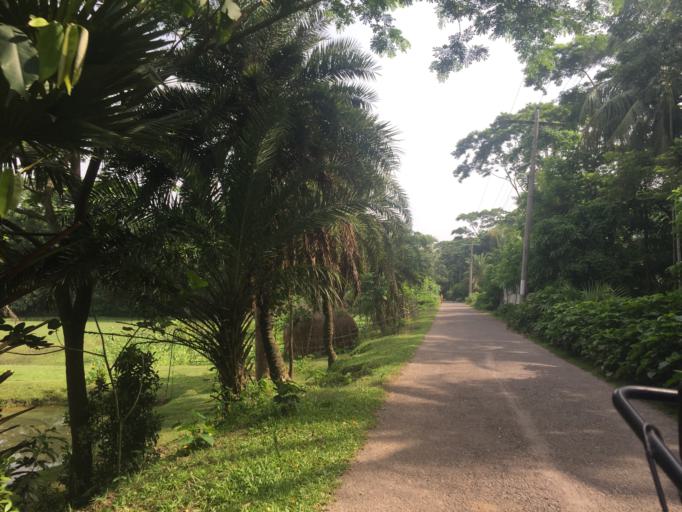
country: BD
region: Barisal
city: Mathba
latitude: 22.2223
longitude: 89.9161
